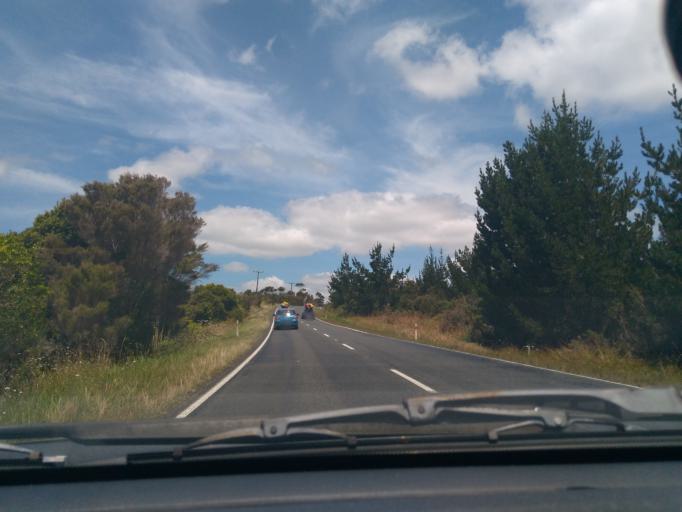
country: NZ
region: Northland
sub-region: Far North District
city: Kerikeri
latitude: -35.1266
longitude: 173.8746
